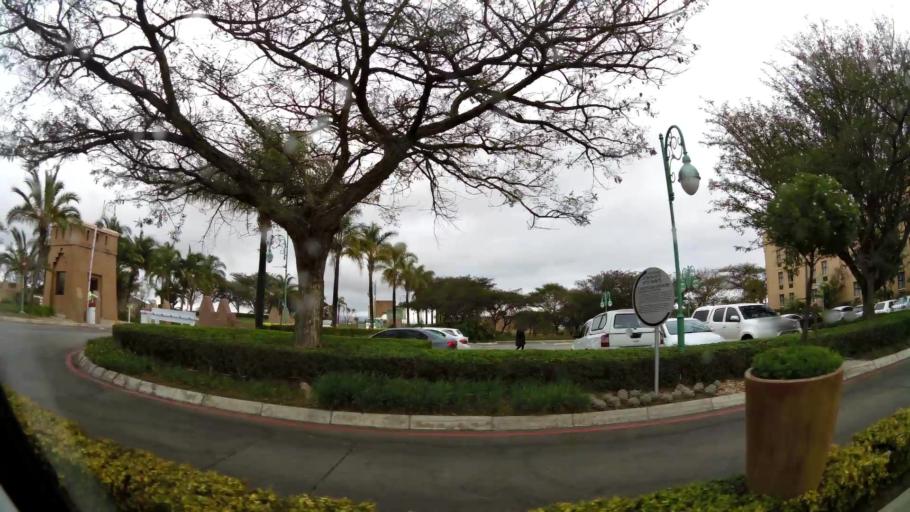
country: ZA
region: Limpopo
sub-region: Capricorn District Municipality
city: Polokwane
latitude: -23.9423
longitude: 29.4229
